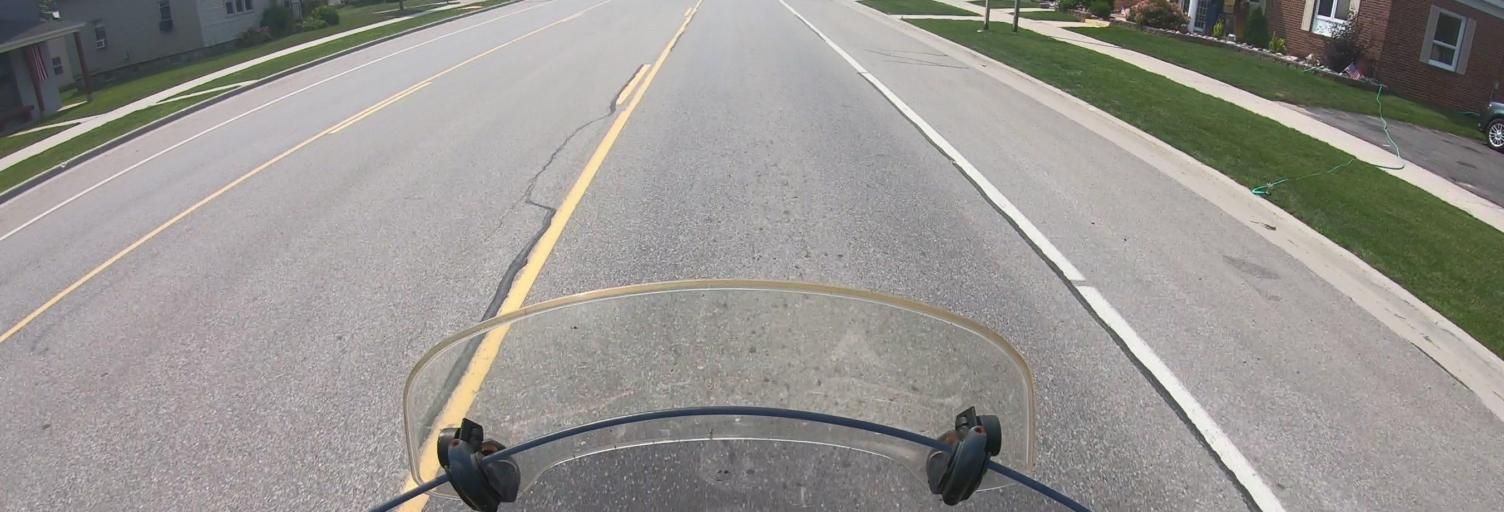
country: US
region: Michigan
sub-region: Luce County
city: Newberry
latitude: 46.3536
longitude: -85.5099
